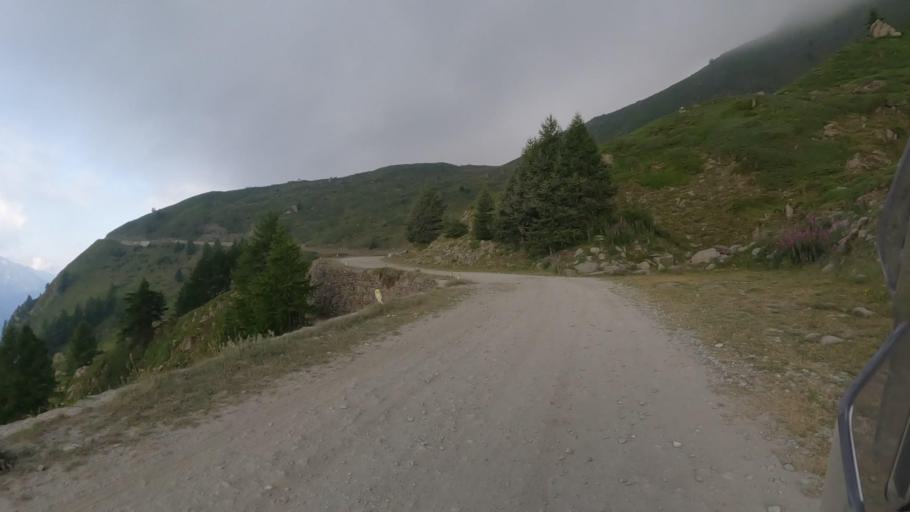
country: IT
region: Piedmont
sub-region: Provincia di Torino
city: Usseaux
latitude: 45.0624
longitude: 7.0068
